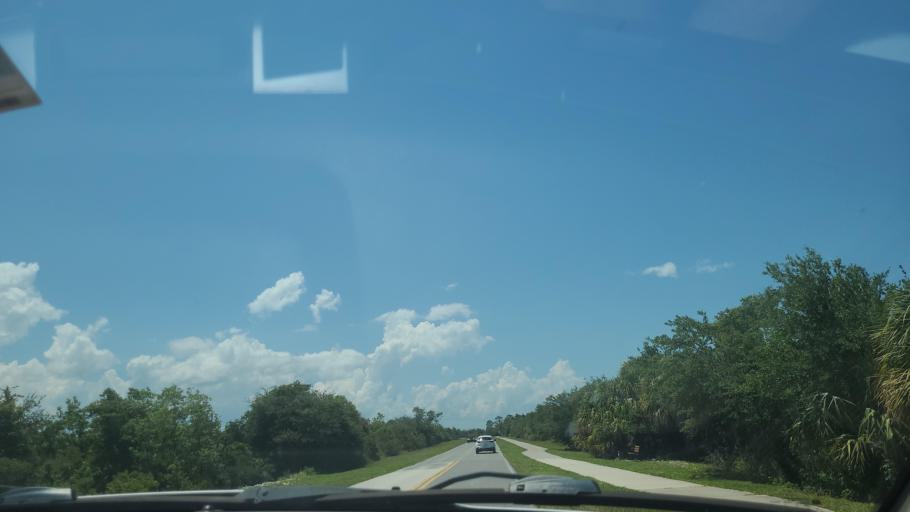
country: US
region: Florida
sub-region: Brevard County
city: Grant-Valkaria
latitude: 27.9652
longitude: -80.5530
